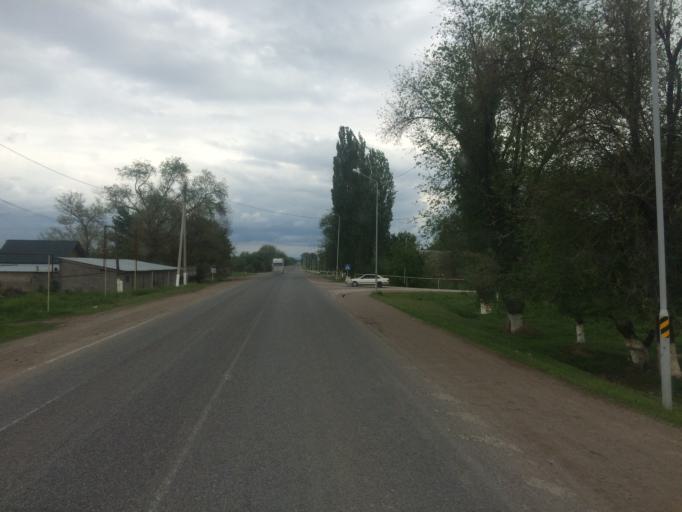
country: KZ
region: Zhambyl
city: Georgiyevka
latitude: 43.2271
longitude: 74.3970
